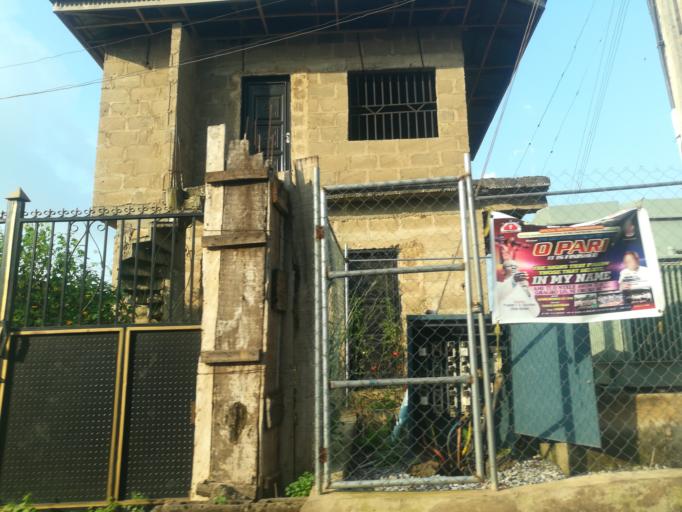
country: NG
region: Oyo
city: Moniya
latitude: 7.4614
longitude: 3.9150
